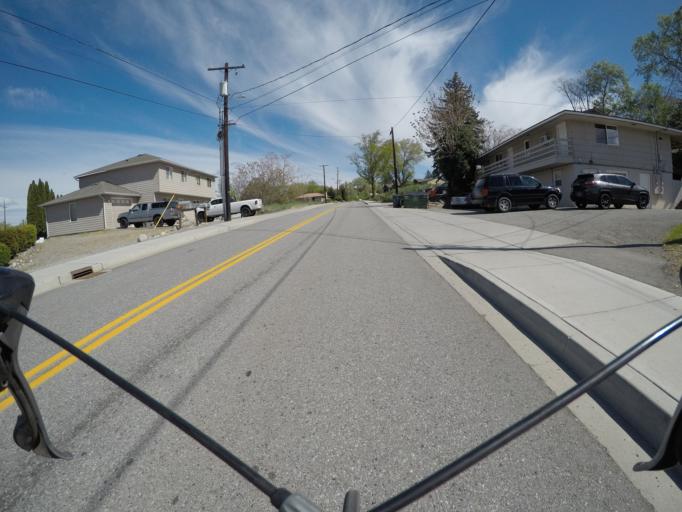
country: US
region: Washington
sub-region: Douglas County
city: East Wenatchee
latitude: 47.4183
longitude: -120.2935
